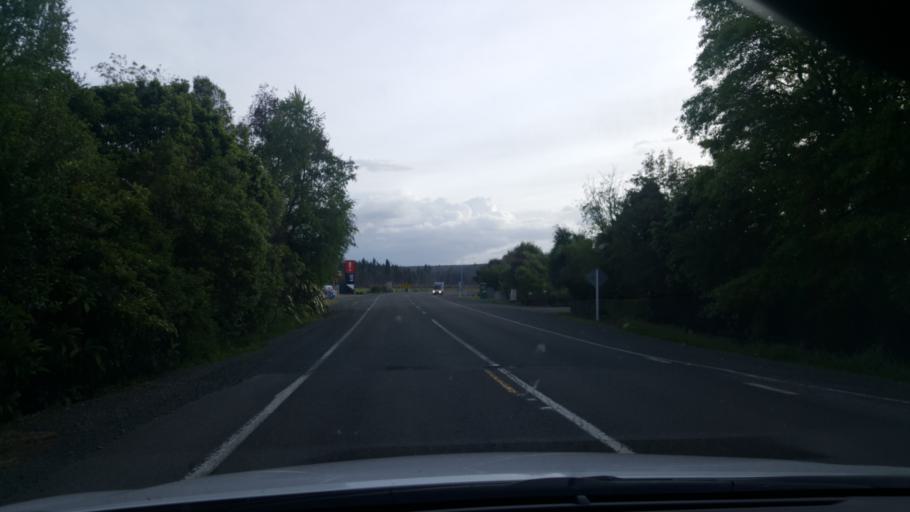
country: NZ
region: Waikato
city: Turangi
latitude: -38.9122
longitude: 175.8981
